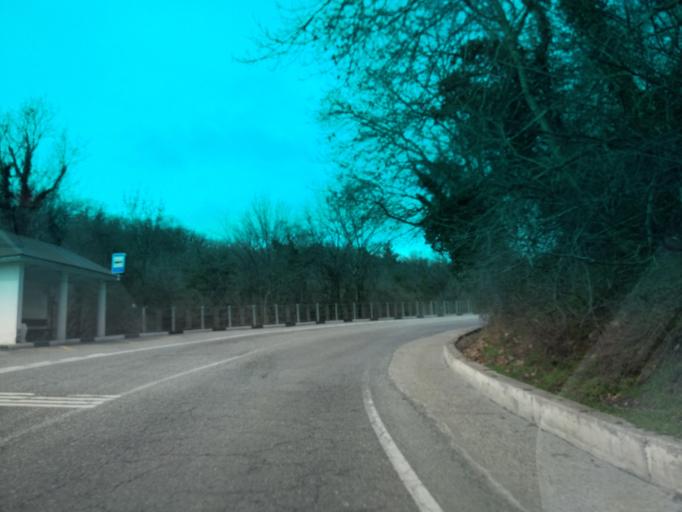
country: RU
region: Krasnodarskiy
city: Shepsi
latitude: 44.0422
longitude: 39.1423
